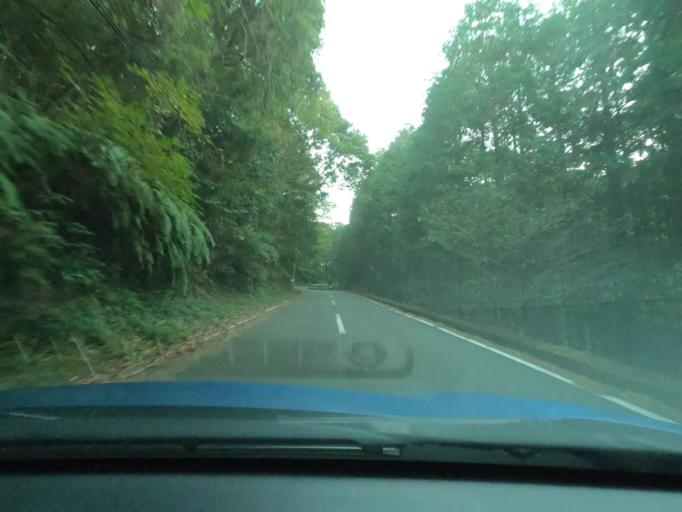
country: JP
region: Kagoshima
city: Satsumasendai
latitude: 31.8191
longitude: 130.4782
